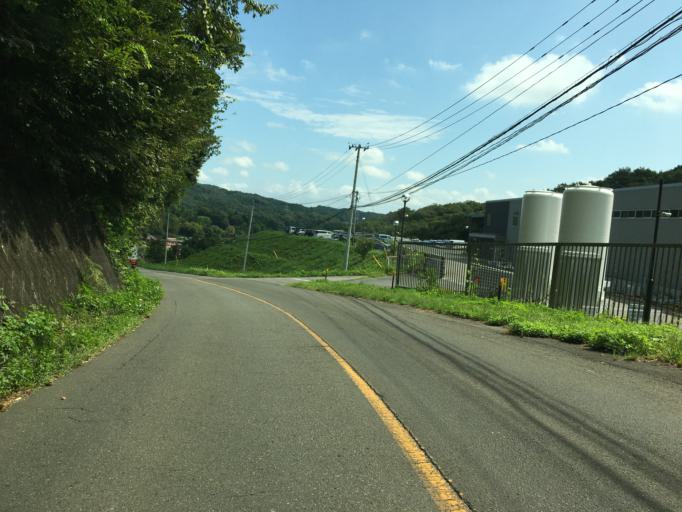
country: JP
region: Fukushima
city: Nihommatsu
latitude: 37.6002
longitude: 140.3872
